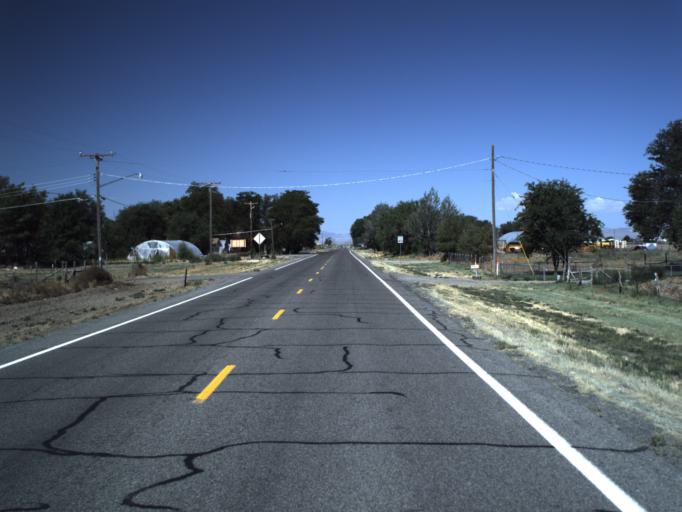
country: US
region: Utah
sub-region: Millard County
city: Delta
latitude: 39.3307
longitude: -112.6649
